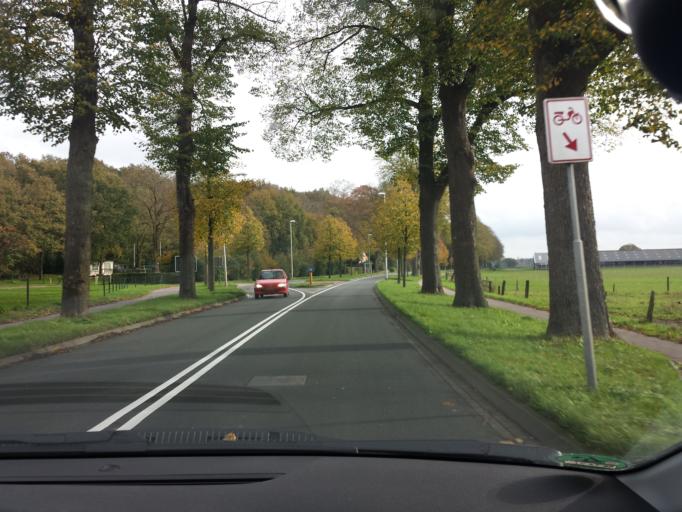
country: NL
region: North Brabant
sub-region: Gemeente Cuijk
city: Cuijk
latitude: 51.7476
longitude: 5.8924
